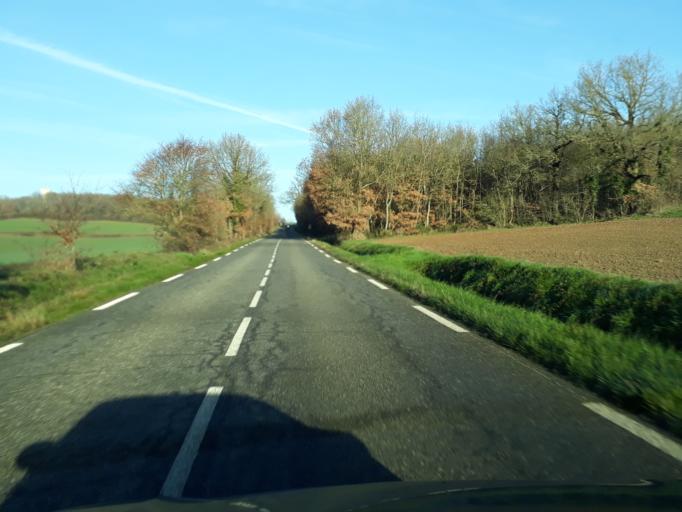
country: FR
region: Midi-Pyrenees
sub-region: Departement du Gers
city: Pujaudran
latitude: 43.5592
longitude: 1.1314
